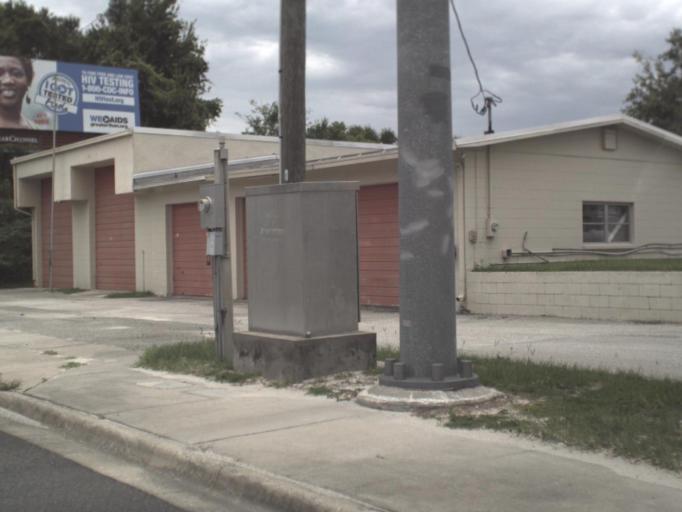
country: US
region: Florida
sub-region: Citrus County
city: Inverness
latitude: 28.8495
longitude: -82.2694
